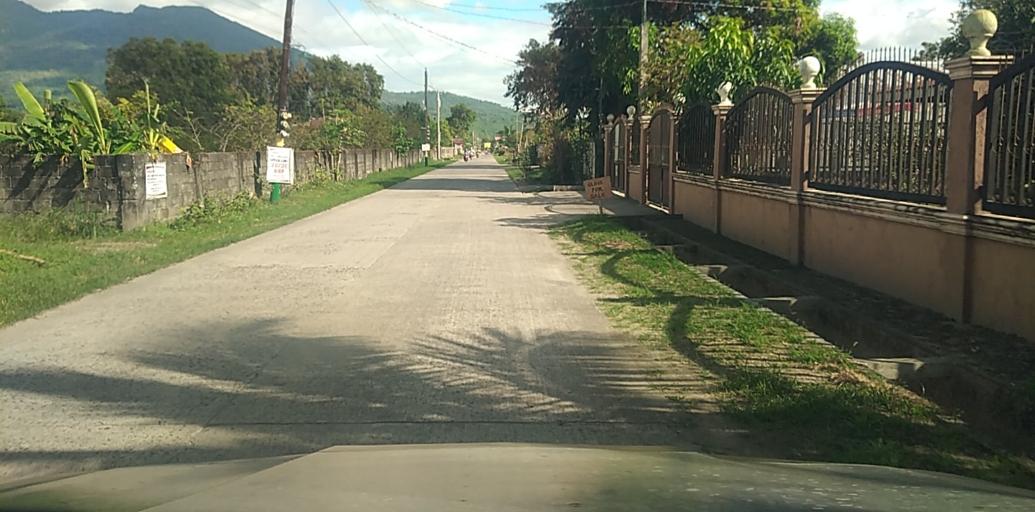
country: PH
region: Central Luzon
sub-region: Province of Pampanga
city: Buensuseso
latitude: 15.1927
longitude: 120.6834
